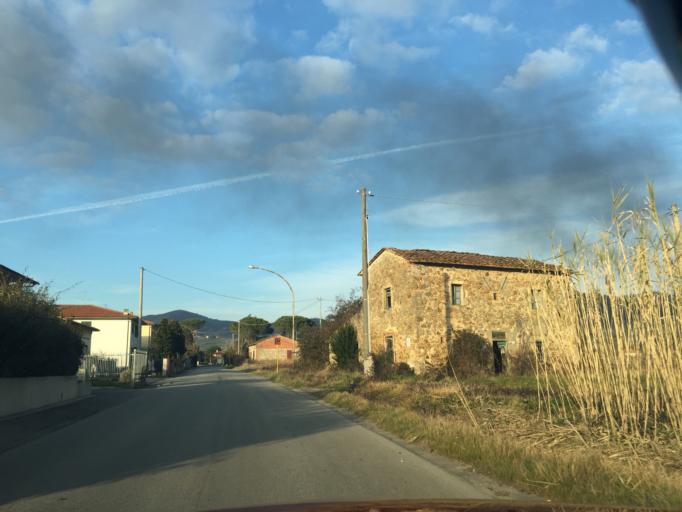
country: IT
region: Tuscany
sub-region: Provincia di Pistoia
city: San Rocco
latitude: 43.8305
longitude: 10.8643
